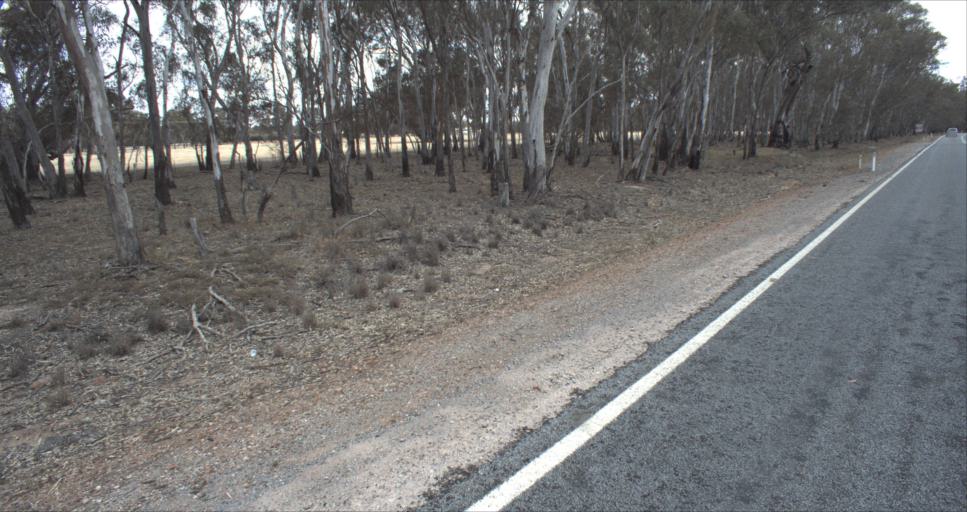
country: AU
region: New South Wales
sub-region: Leeton
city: Leeton
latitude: -34.6283
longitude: 146.3776
